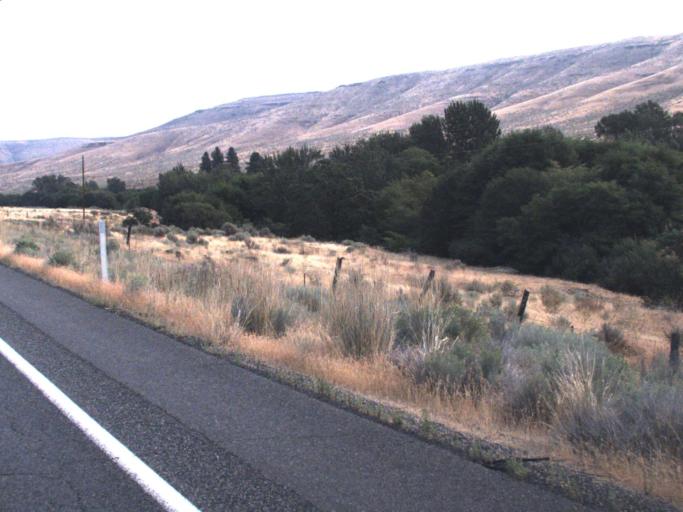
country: US
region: Washington
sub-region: Yakima County
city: Toppenish
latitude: 46.1300
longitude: -120.5288
